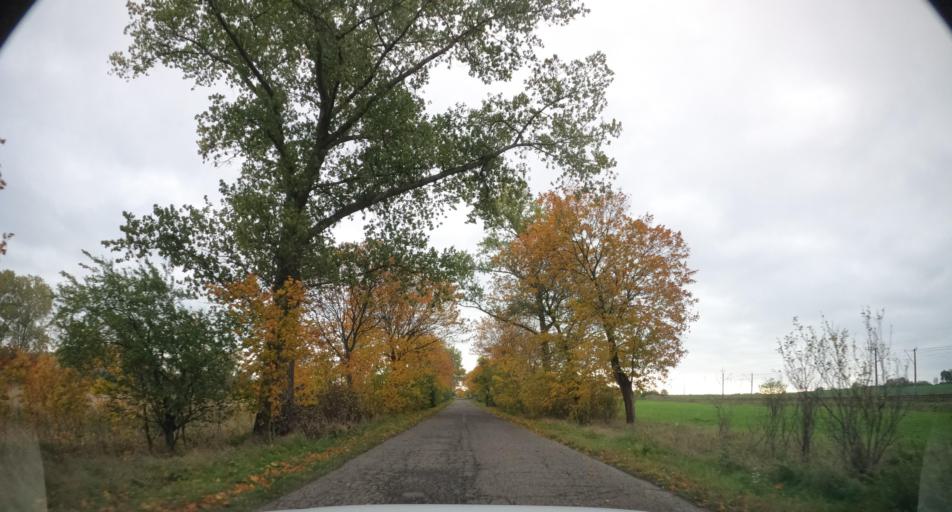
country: PL
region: West Pomeranian Voivodeship
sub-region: Powiat kamienski
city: Wolin
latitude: 53.8692
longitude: 14.5855
